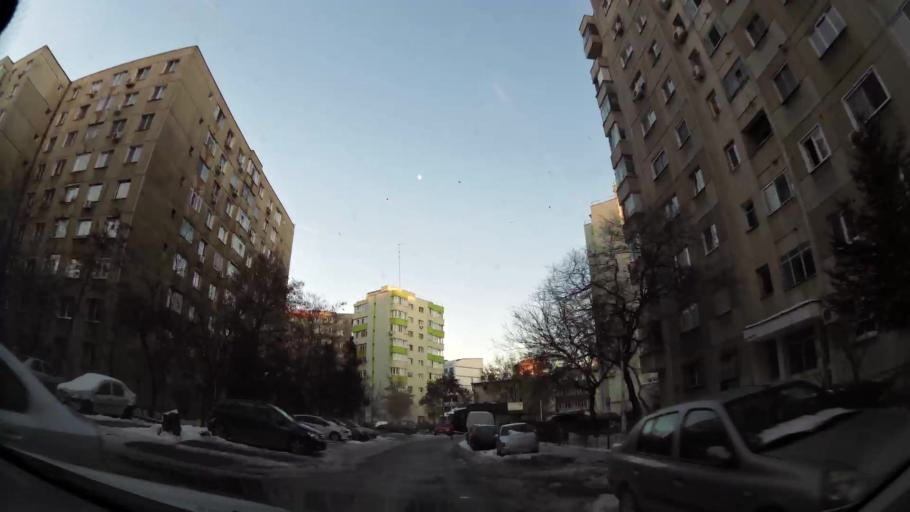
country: RO
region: Ilfov
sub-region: Comuna Fundeni-Dobroesti
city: Fundeni
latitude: 44.4452
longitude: 26.1452
